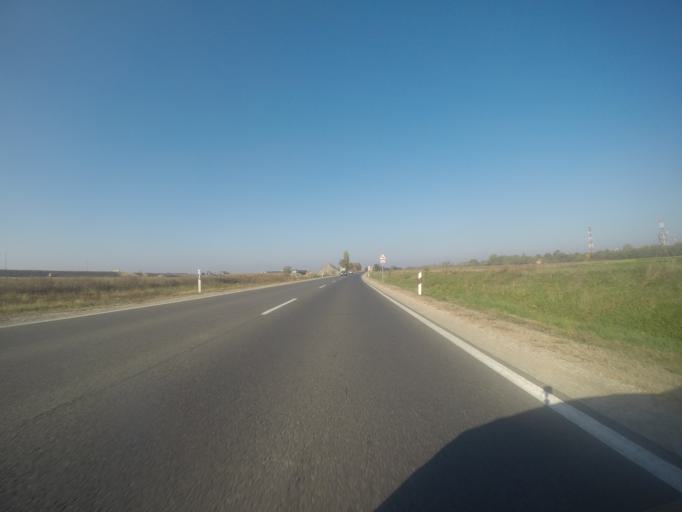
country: HU
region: Fejer
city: Ercsi
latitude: 47.2850
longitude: 18.8733
